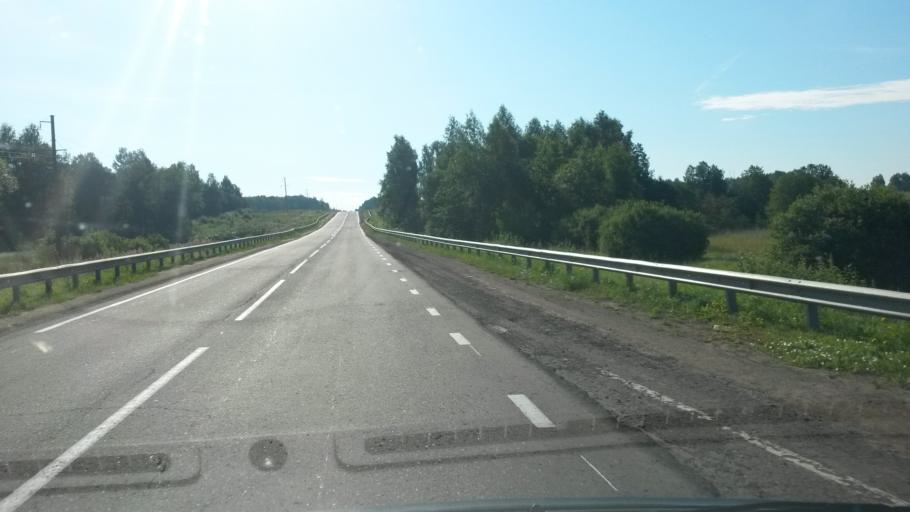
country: RU
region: Jaroslavl
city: Gavrilov-Yam
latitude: 57.2634
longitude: 40.0258
